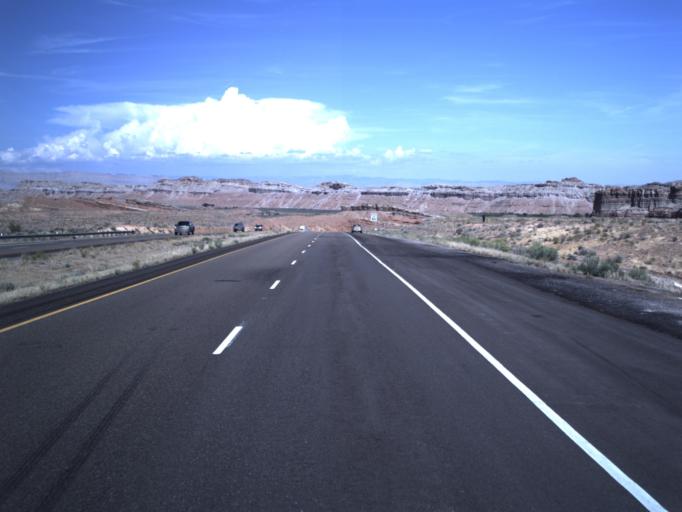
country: US
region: Utah
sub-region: Carbon County
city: East Carbon City
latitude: 38.9215
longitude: -110.4274
